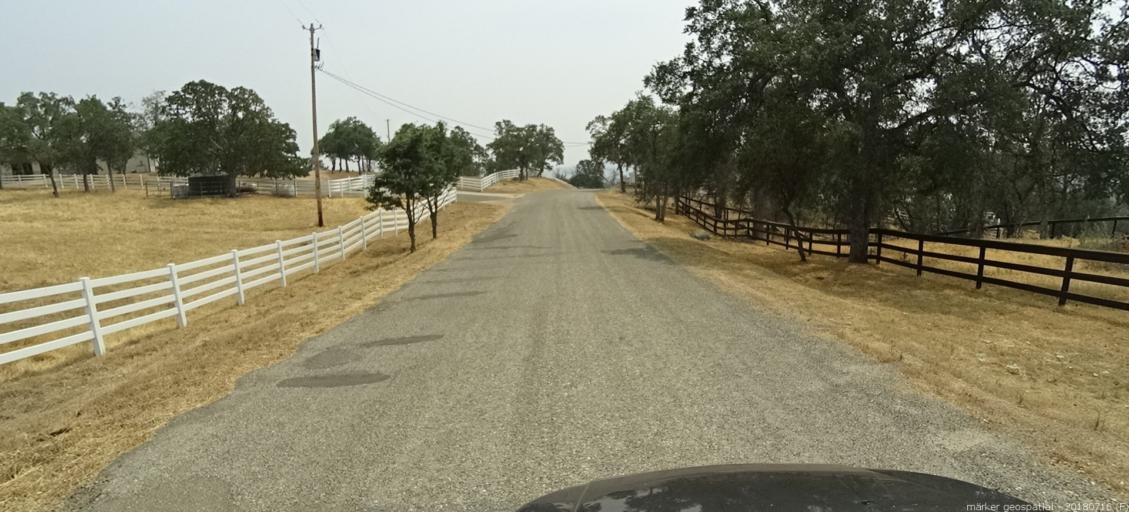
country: US
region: California
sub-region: Madera County
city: Yosemite Lakes
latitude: 37.2376
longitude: -119.8015
